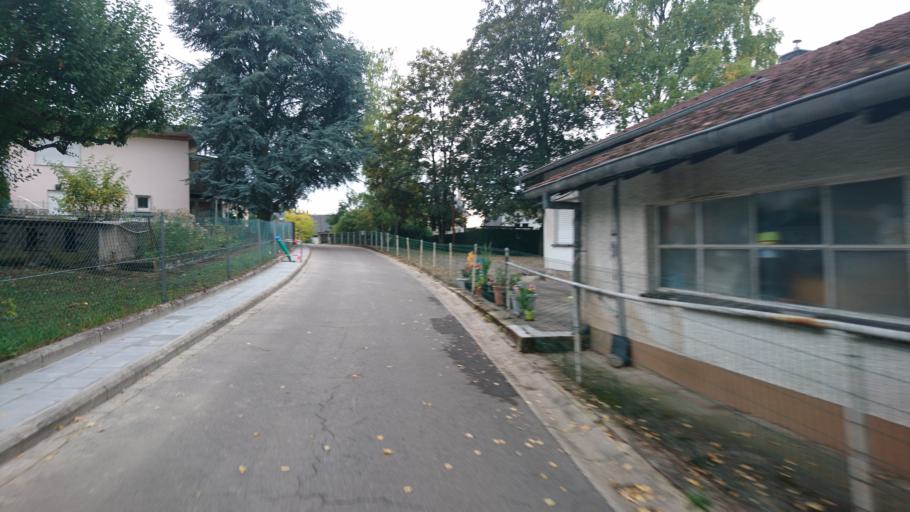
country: LU
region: Luxembourg
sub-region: Canton de Luxembourg
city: Walferdange
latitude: 49.6616
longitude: 6.1381
